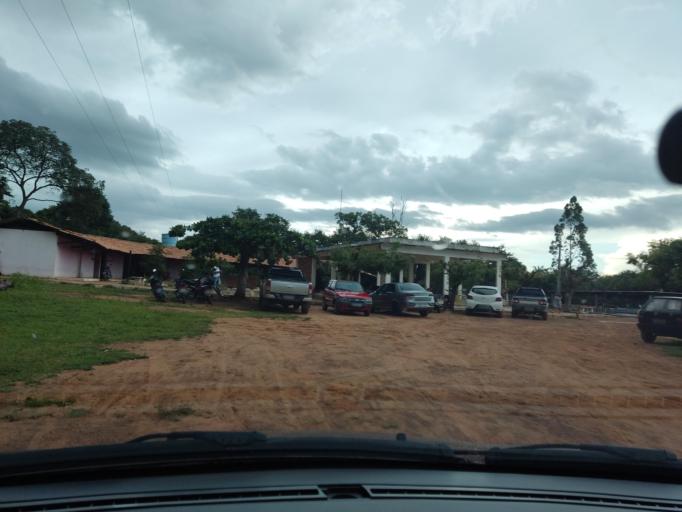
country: BR
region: Piaui
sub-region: Valenca Do Piaui
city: Valenca do Piaui
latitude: -6.3531
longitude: -41.7075
